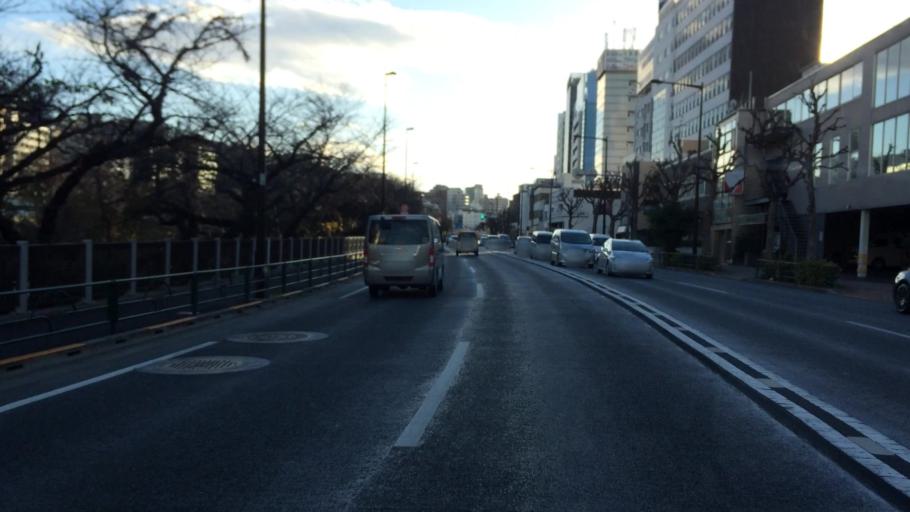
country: JP
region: Tokyo
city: Tokyo
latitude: 35.6969
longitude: 139.7397
